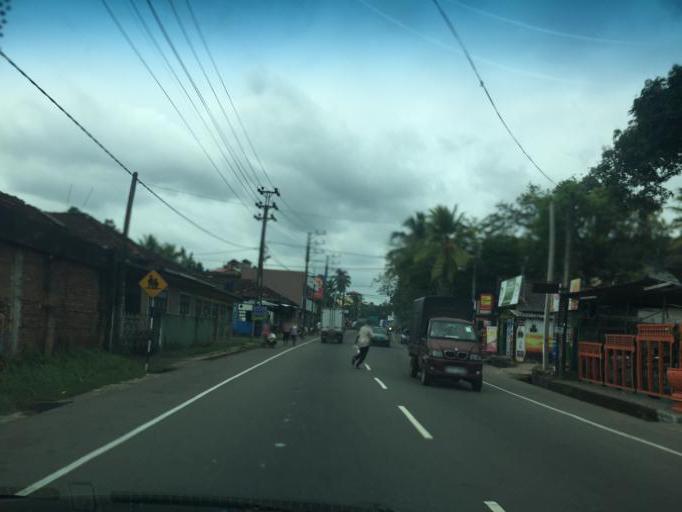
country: LK
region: Western
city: Horana South
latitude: 6.7184
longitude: 80.0691
